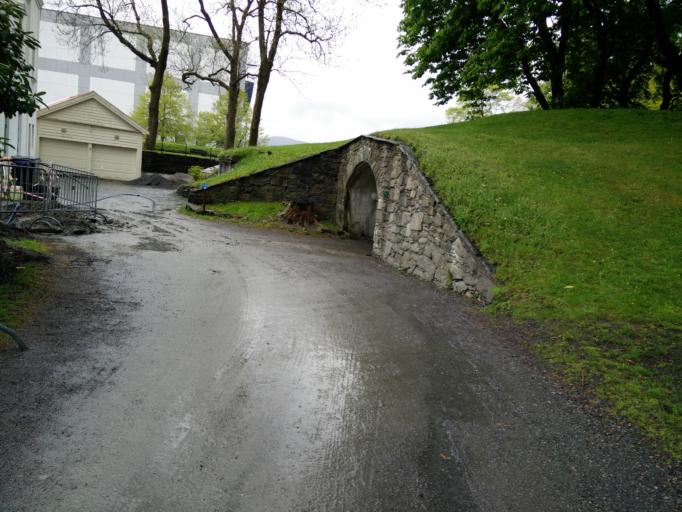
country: NO
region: Hordaland
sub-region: Bergen
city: Bergen
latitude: 60.4009
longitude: 5.3181
